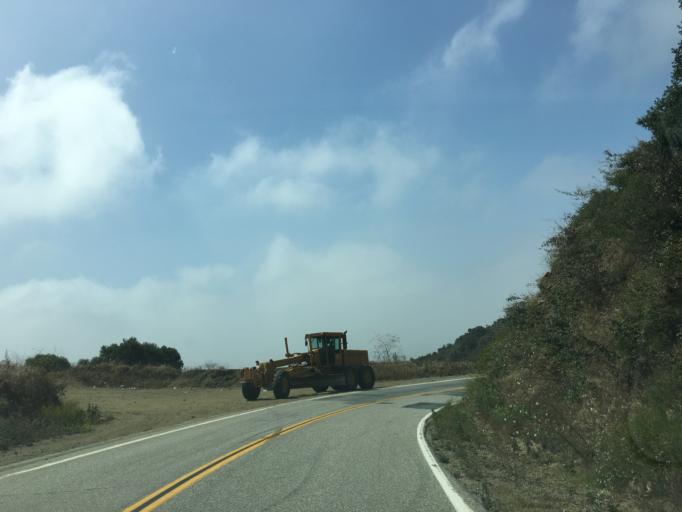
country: US
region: California
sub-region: Los Angeles County
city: Glendora
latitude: 34.1692
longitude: -117.8447
